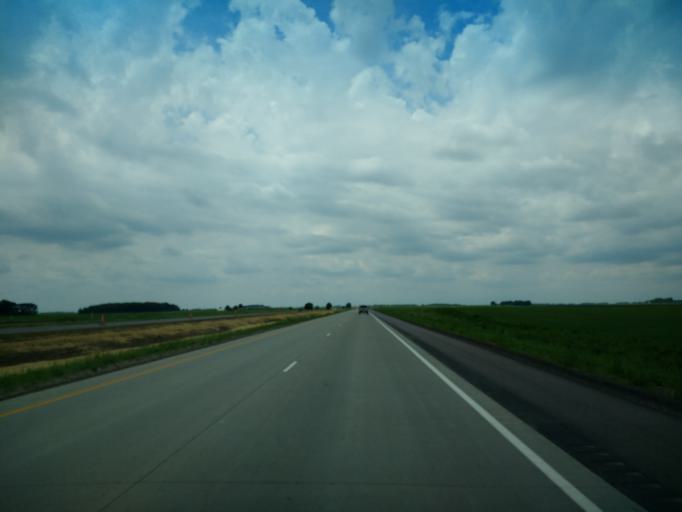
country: US
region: Minnesota
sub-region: Cottonwood County
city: Mountain Lake
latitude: 43.9278
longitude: -94.9659
